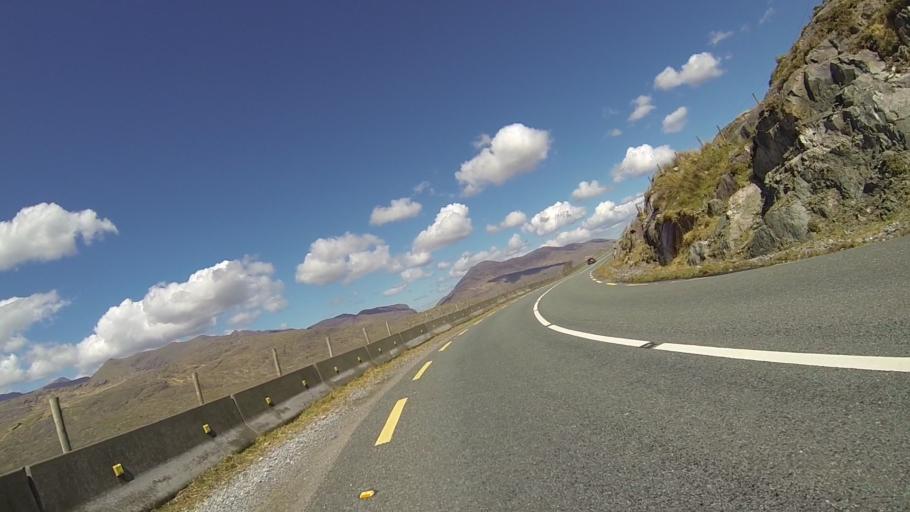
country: IE
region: Munster
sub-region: Ciarrai
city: Kenmare
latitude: 51.9407
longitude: -9.6540
